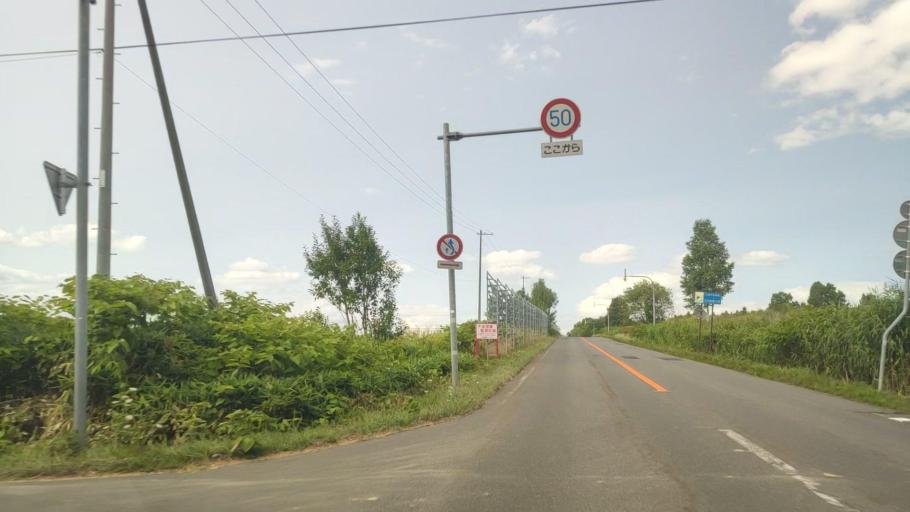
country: JP
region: Hokkaido
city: Nayoro
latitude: 44.2461
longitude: 142.4156
